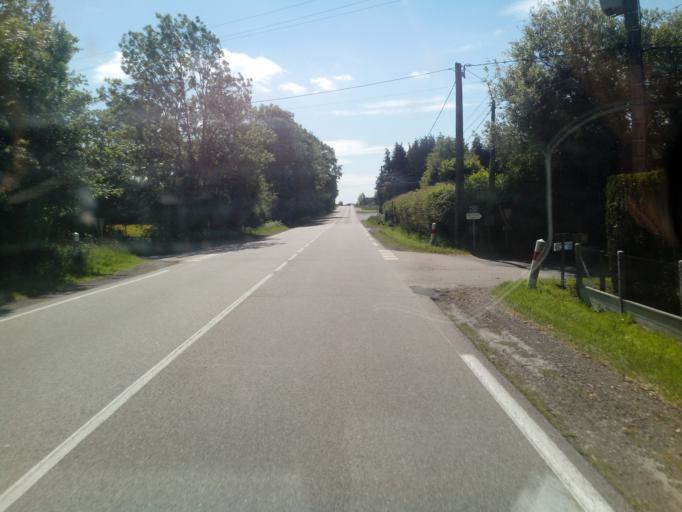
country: FR
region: Haute-Normandie
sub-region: Departement de l'Eure
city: Beuzeville
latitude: 49.3557
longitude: 0.3887
